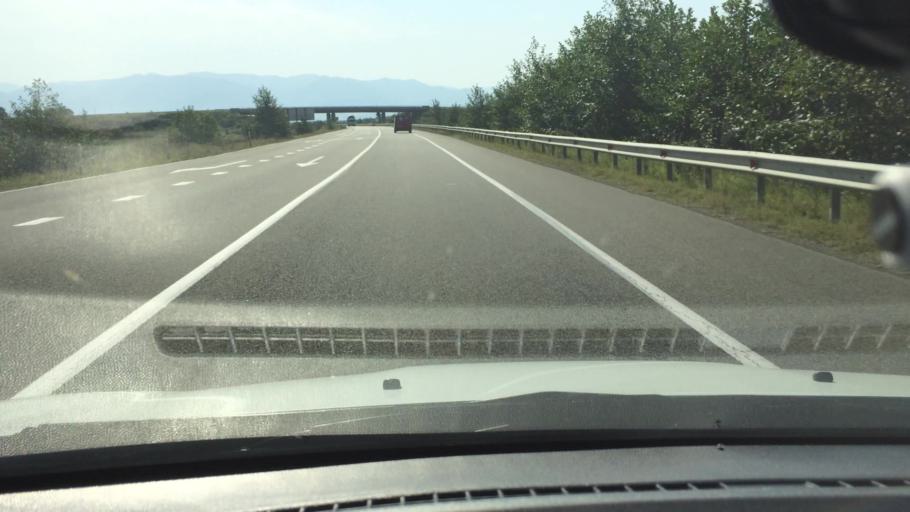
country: GE
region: Guria
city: Urek'i
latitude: 41.9208
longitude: 41.7746
